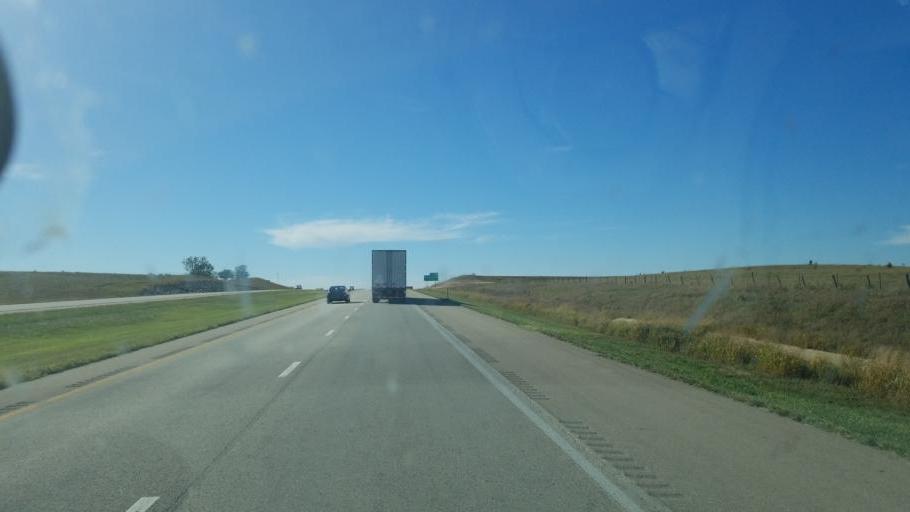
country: US
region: Kansas
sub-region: Saline County
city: Salina
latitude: 38.8781
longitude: -97.7420
